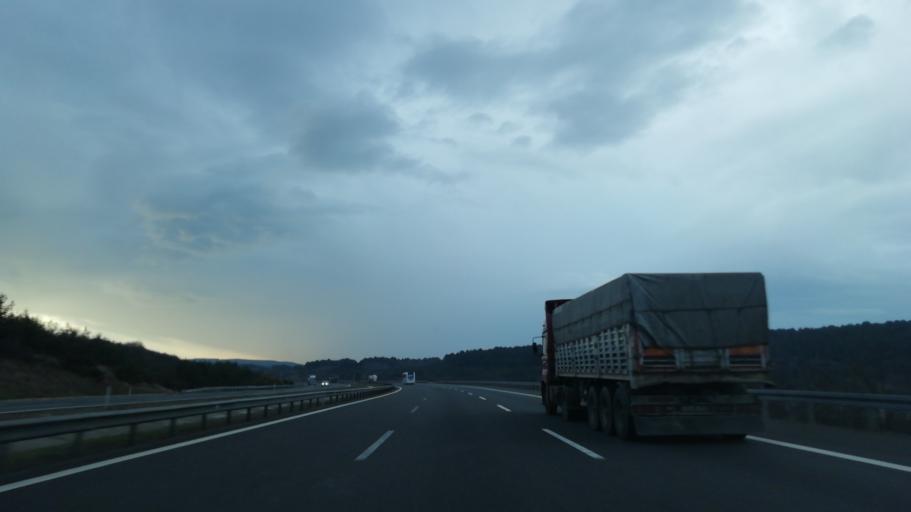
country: TR
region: Bolu
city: Yenicaga
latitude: 40.7539
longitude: 31.9209
